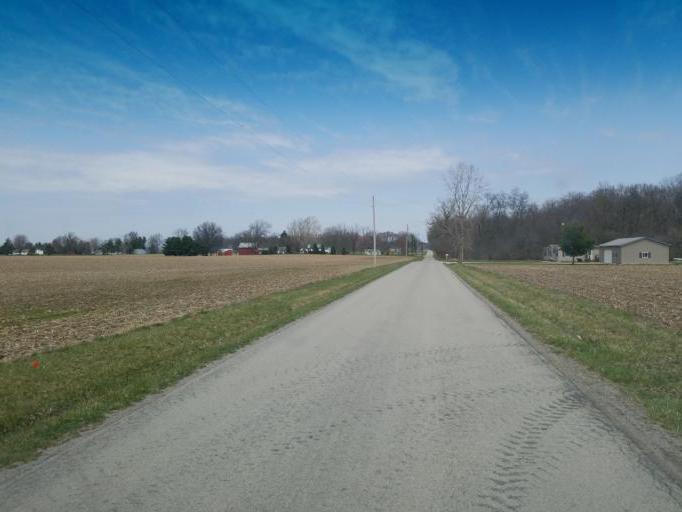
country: US
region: Ohio
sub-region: Wyandot County
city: Upper Sandusky
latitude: 40.8533
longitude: -83.2561
